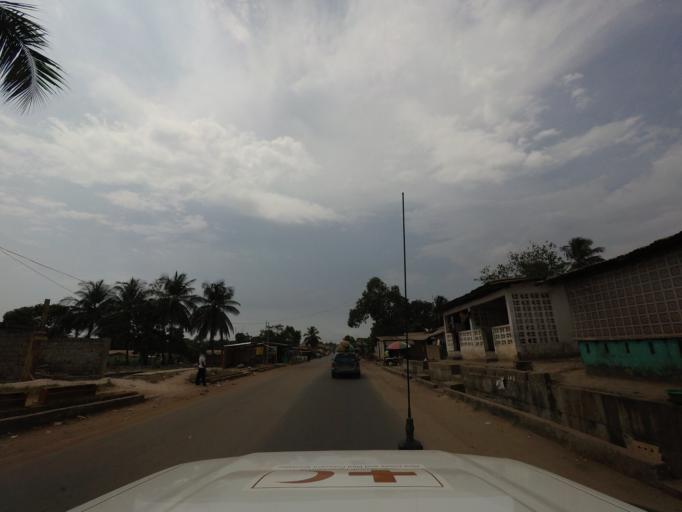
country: LR
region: Montserrado
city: Monrovia
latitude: 6.2948
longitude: -10.6825
